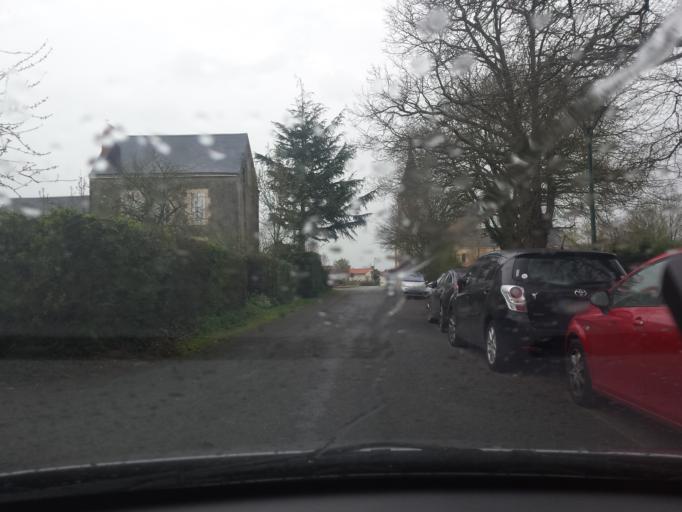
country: FR
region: Pays de la Loire
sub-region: Departement de la Vendee
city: Sainte-Hermine
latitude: 46.5865
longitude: -1.0949
